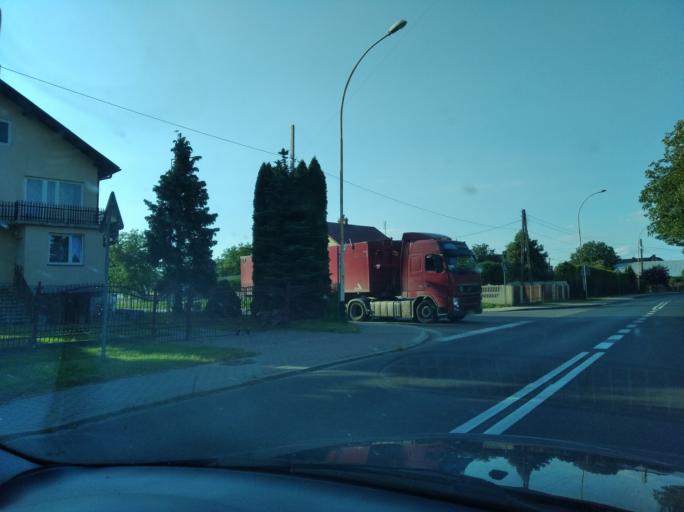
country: PL
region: Subcarpathian Voivodeship
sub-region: Powiat lezajski
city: Lezajsk
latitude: 50.2733
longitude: 22.4258
